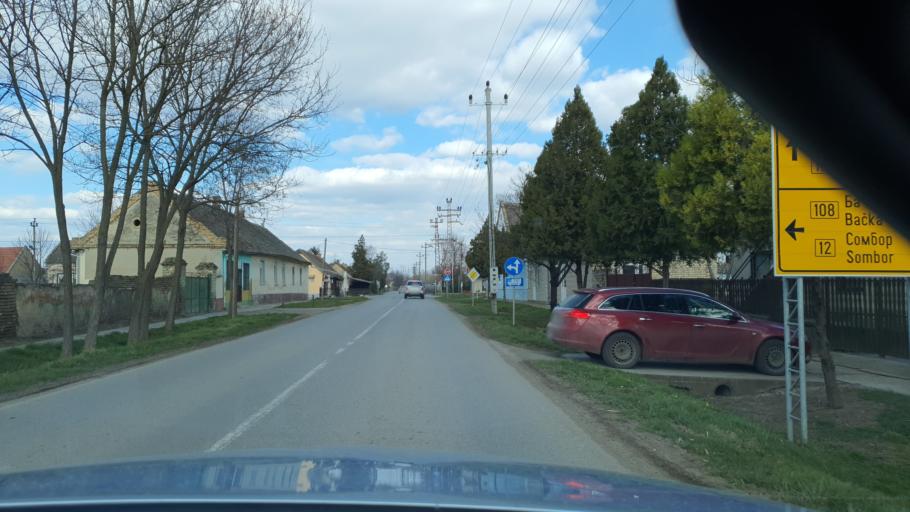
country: RS
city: Ravno Selo
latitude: 45.4510
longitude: 19.6130
